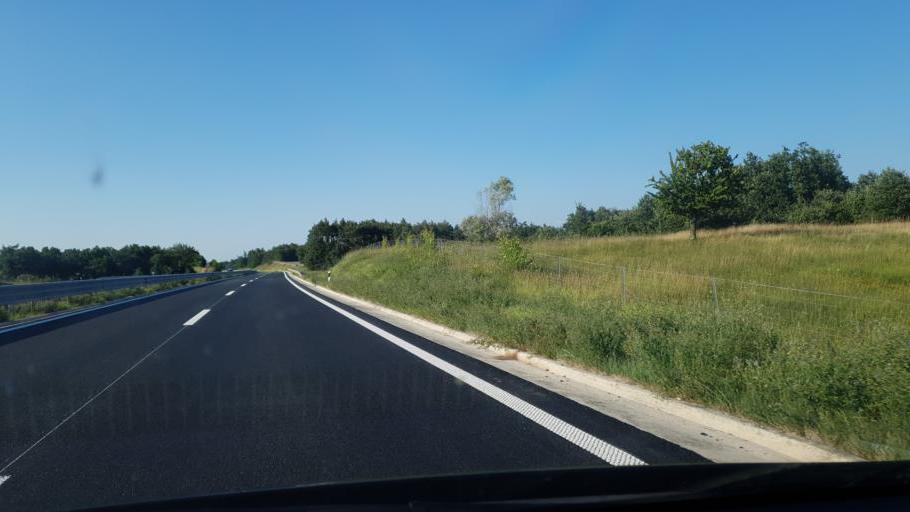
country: HR
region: Istarska
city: Pazin
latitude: 45.1611
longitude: 13.8858
